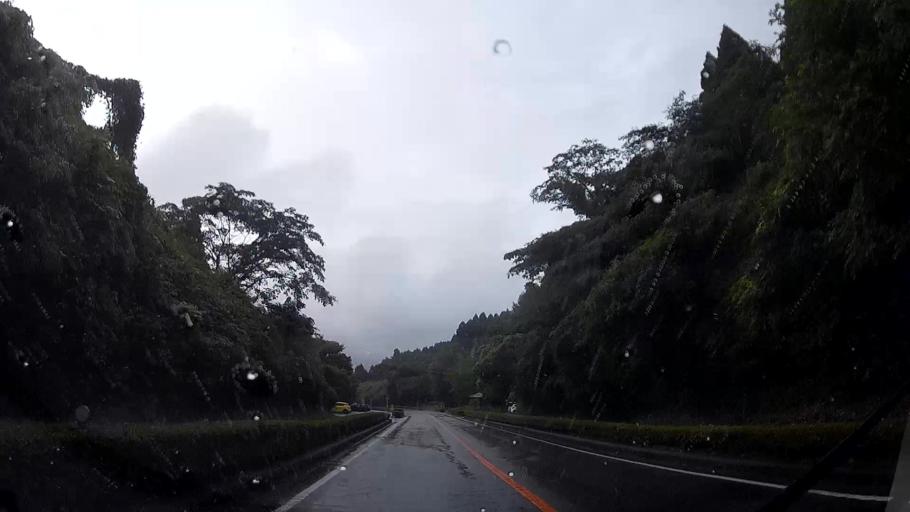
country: JP
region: Kumamoto
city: Aso
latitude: 32.8580
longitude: 131.0071
